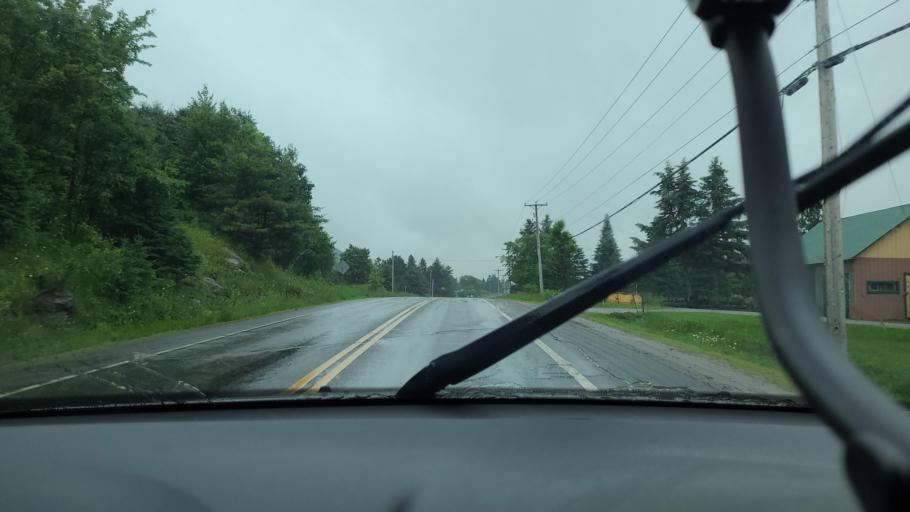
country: CA
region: Quebec
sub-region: Outaouais
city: Saint-Andre-Avellin
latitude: 45.7089
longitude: -75.0536
